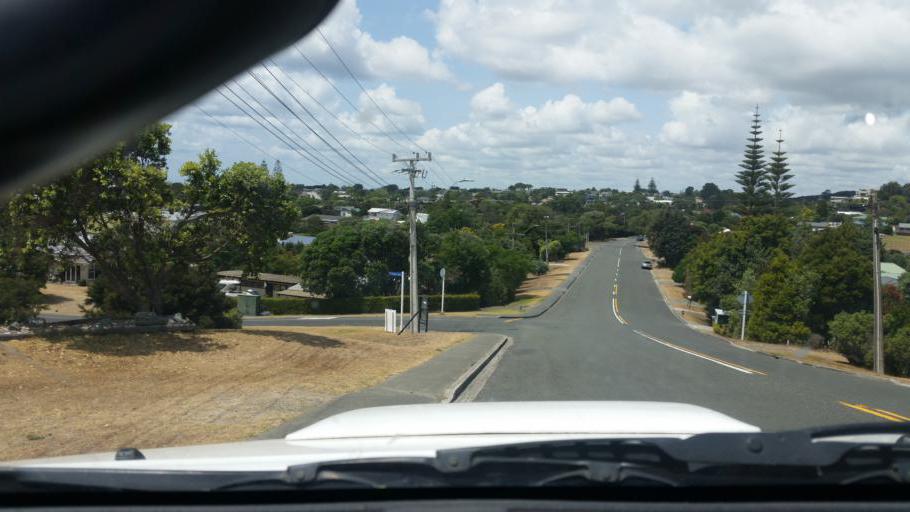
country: NZ
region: Auckland
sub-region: Auckland
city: Wellsford
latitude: -36.0882
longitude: 174.5834
